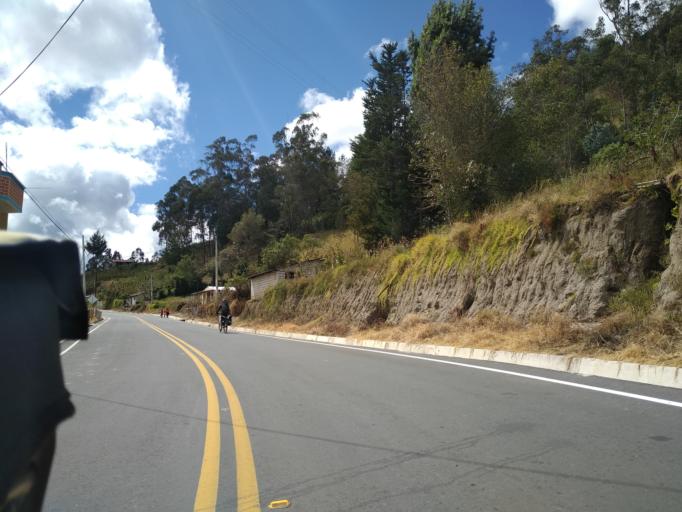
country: EC
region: Cotopaxi
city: Saquisili
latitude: -0.7076
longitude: -78.8857
